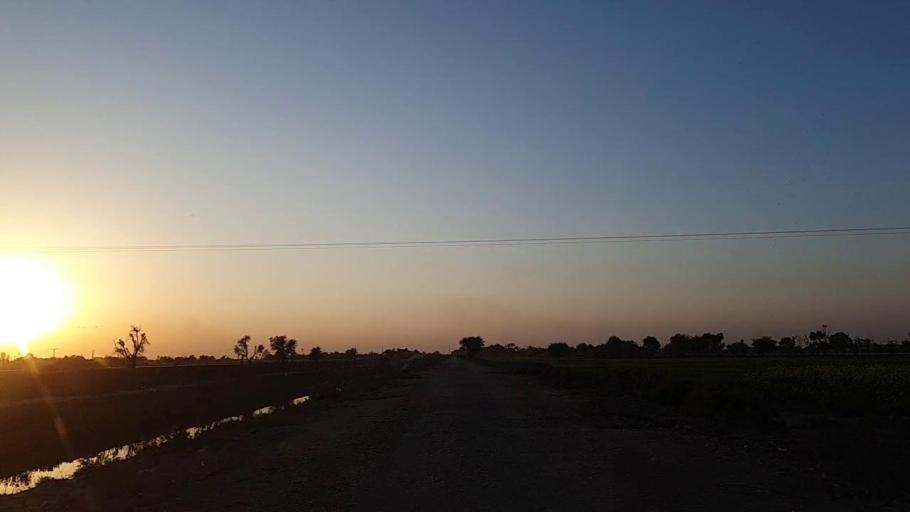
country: PK
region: Sindh
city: Jam Sahib
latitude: 26.3106
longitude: 68.6586
